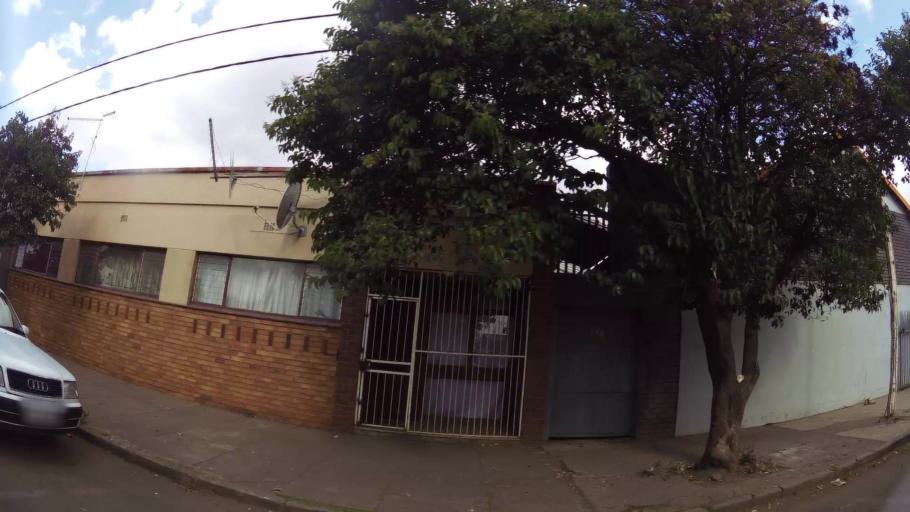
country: ZA
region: Mpumalanga
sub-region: Nkangala District Municipality
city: Delmas
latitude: -26.1496
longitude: 28.6849
